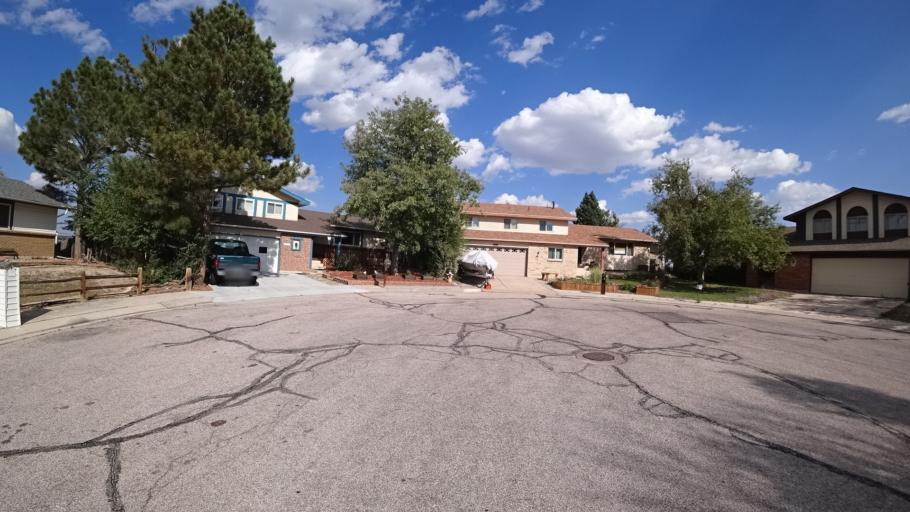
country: US
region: Colorado
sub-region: El Paso County
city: Cimarron Hills
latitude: 38.8764
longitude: -104.7285
